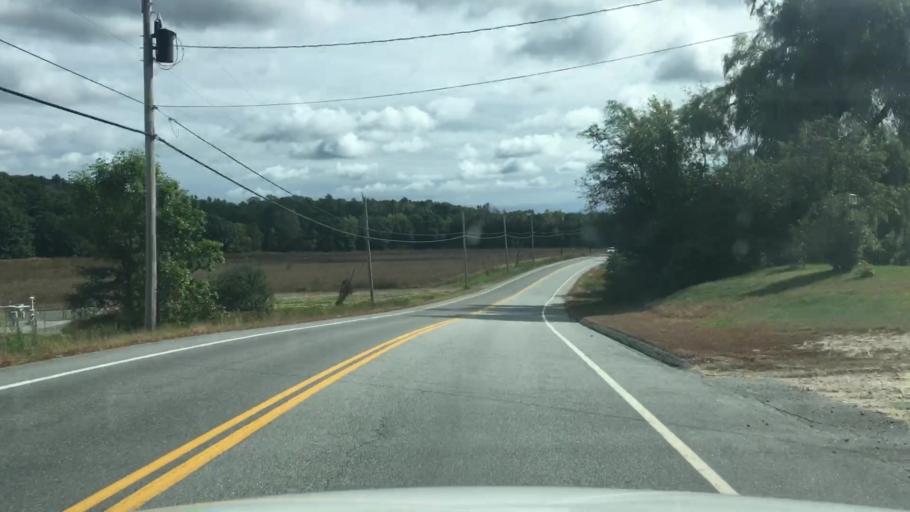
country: US
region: Maine
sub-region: Androscoggin County
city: Lisbon
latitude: 44.0177
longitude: -70.1716
